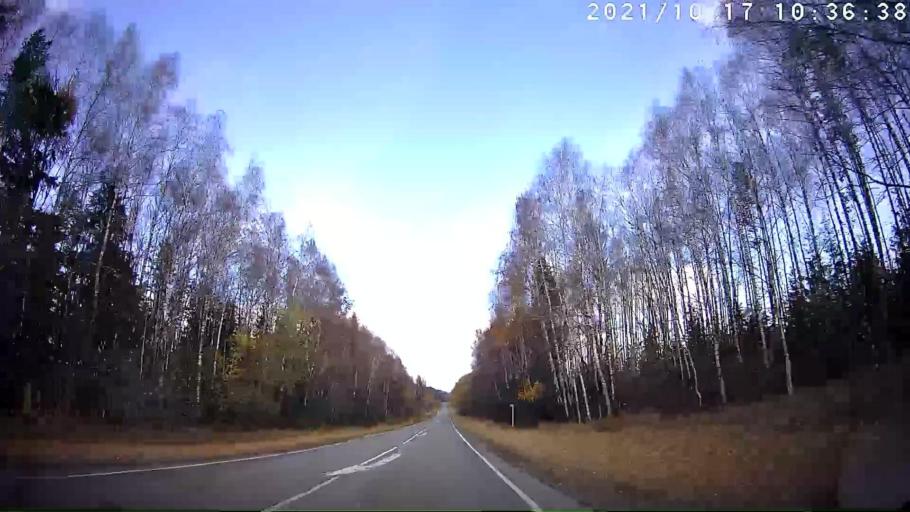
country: RU
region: Mariy-El
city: Kuzhener
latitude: 56.9530
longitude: 48.7500
